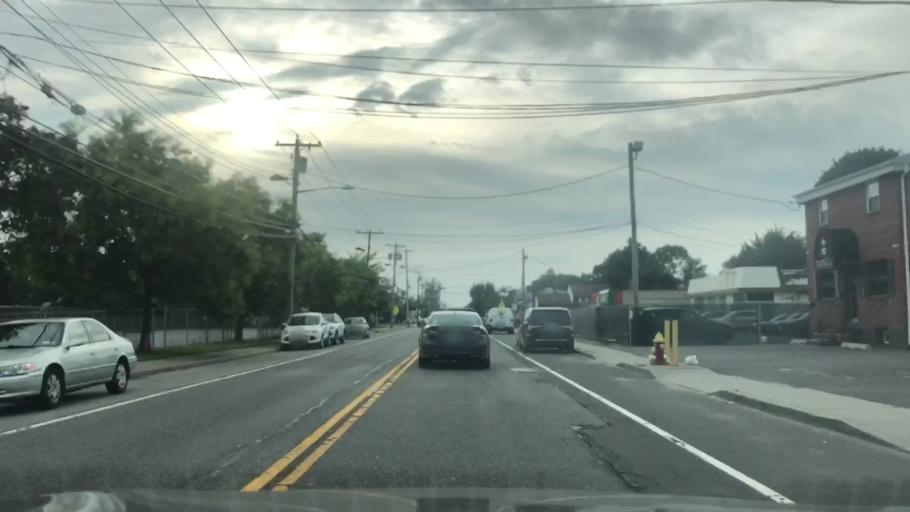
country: US
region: New York
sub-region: Nassau County
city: North Bellmore
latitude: 40.6917
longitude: -73.5294
